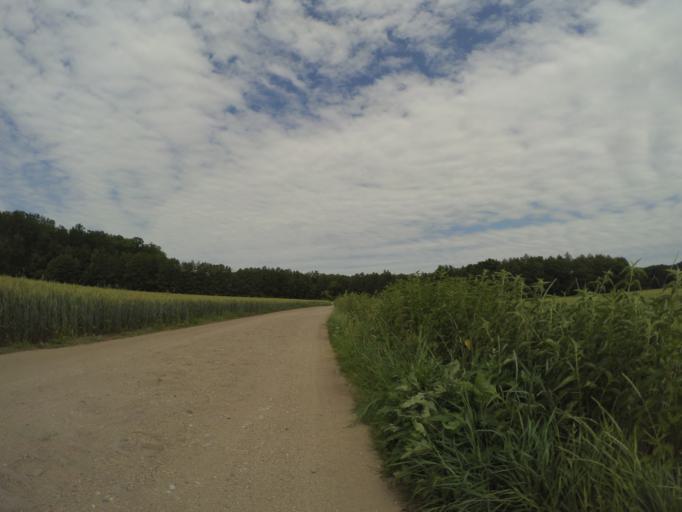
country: CZ
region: Central Bohemia
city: Celakovice
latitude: 50.1756
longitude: 14.7846
